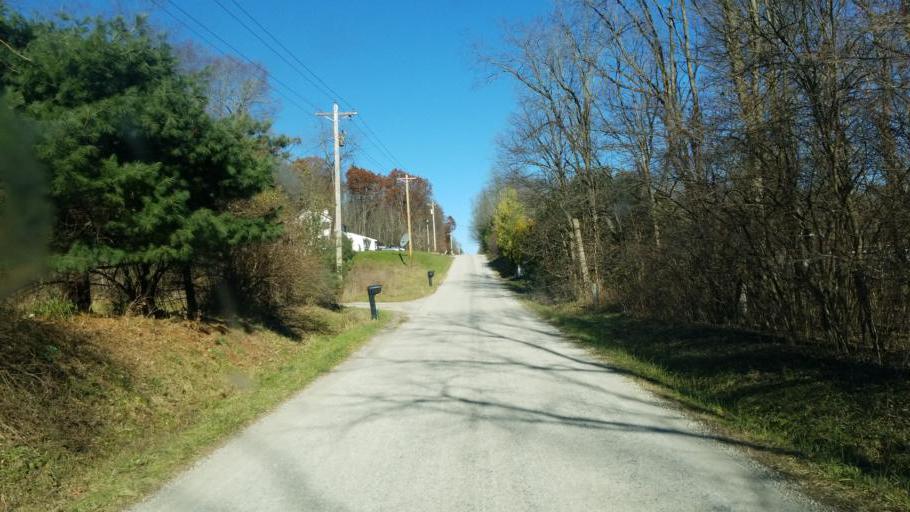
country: US
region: Ohio
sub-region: Ashland County
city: Ashland
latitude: 40.8533
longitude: -82.3877
